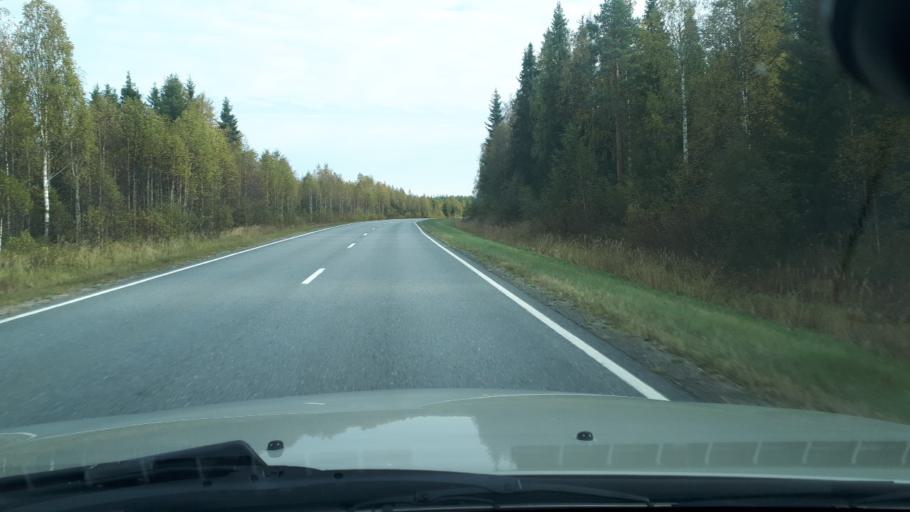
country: FI
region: Lapland
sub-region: Rovaniemi
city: Ranua
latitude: 65.9772
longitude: 26.1213
